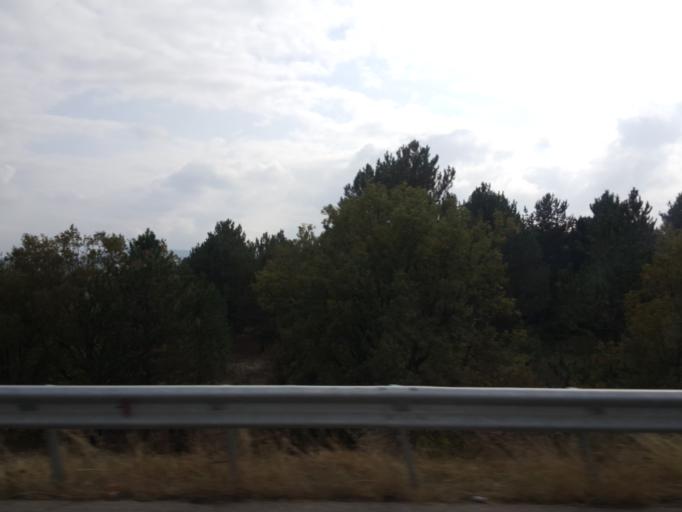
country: TR
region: Sinop
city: Sarayduzu
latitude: 41.3410
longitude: 34.7966
